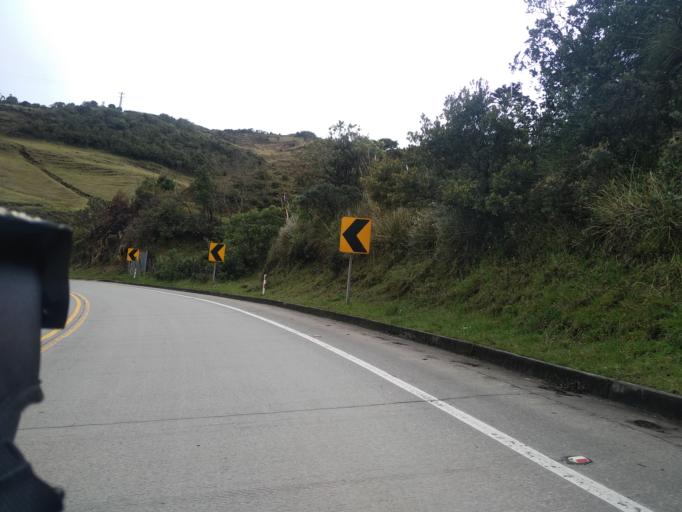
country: EC
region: Loja
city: Catamayo
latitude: -3.8480
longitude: -79.2869
